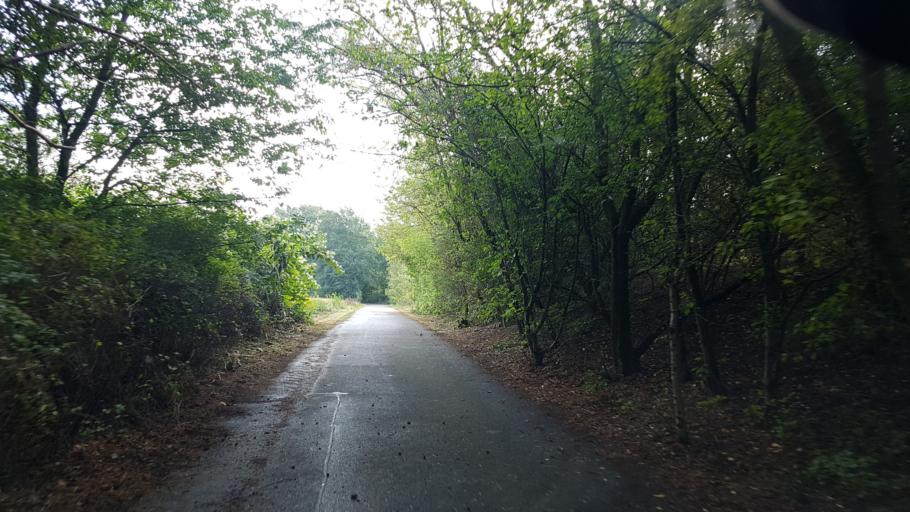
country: DE
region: Brandenburg
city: Plessa
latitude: 51.5286
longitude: 13.6417
